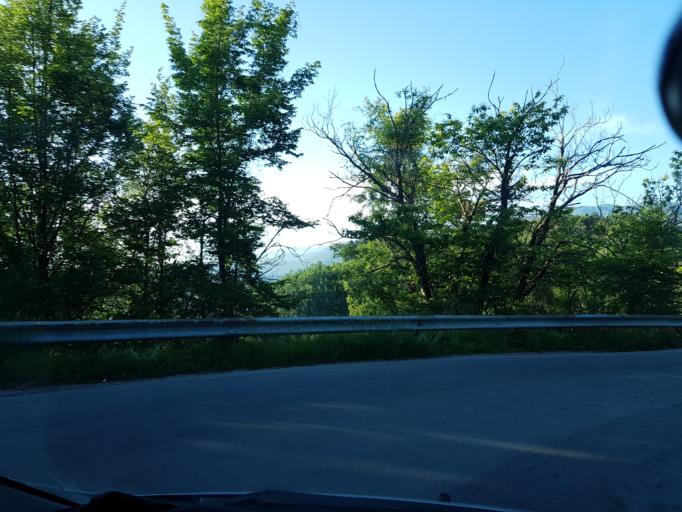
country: IT
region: Tuscany
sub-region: Provincia di Lucca
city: Minucciano
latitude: 44.1789
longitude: 10.1981
